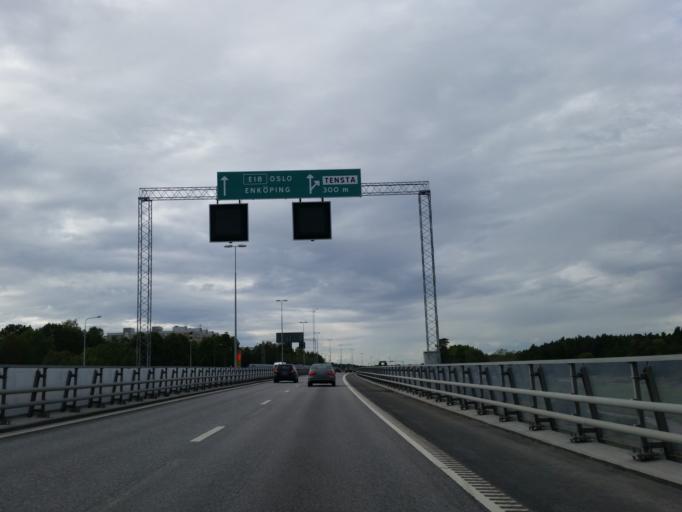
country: SE
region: Stockholm
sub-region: Stockholms Kommun
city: Kista
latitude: 59.3943
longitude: 17.9217
